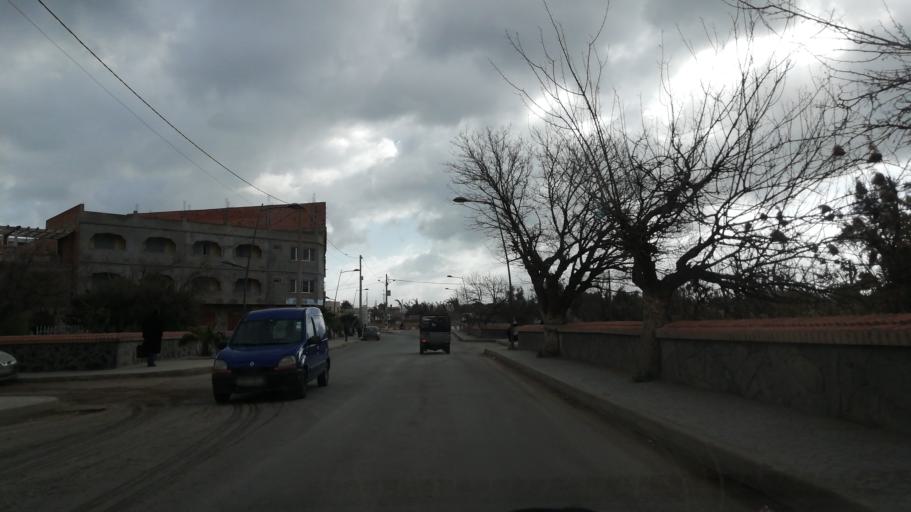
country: DZ
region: Oran
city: Sidi ech Chahmi
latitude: 35.6565
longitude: -0.5265
